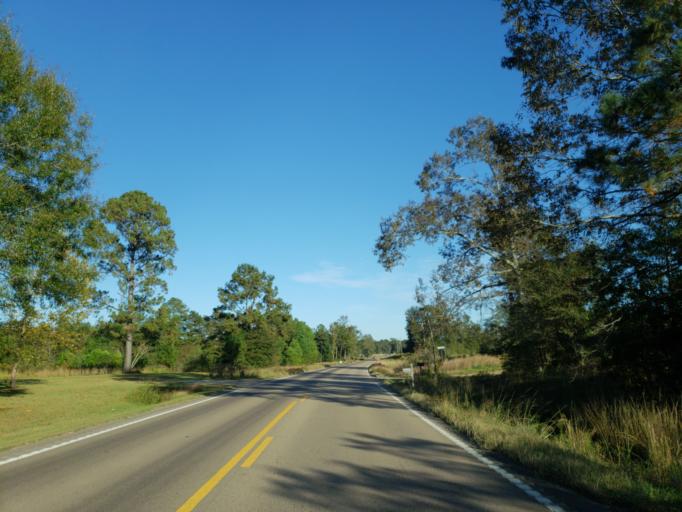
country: US
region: Mississippi
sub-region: Perry County
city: Richton
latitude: 31.3756
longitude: -88.8485
